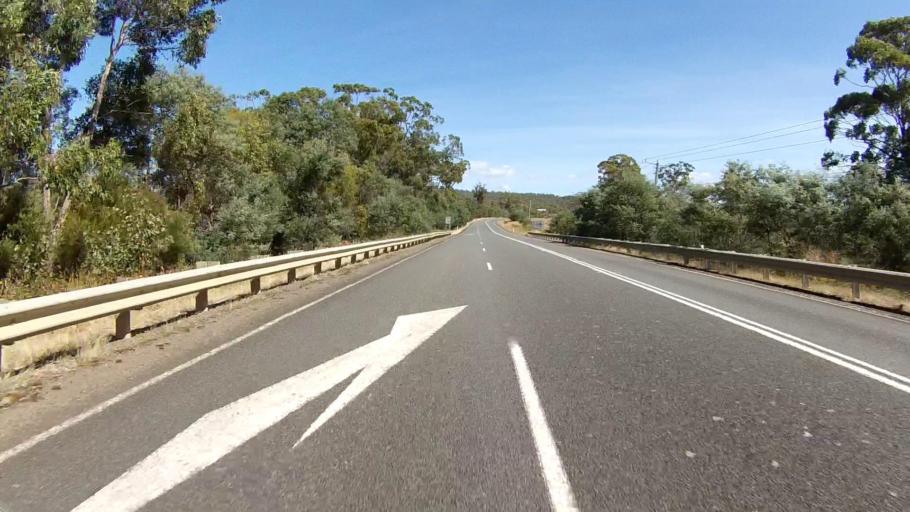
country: AU
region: Tasmania
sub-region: Sorell
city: Sorell
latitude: -42.5761
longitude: 147.8184
